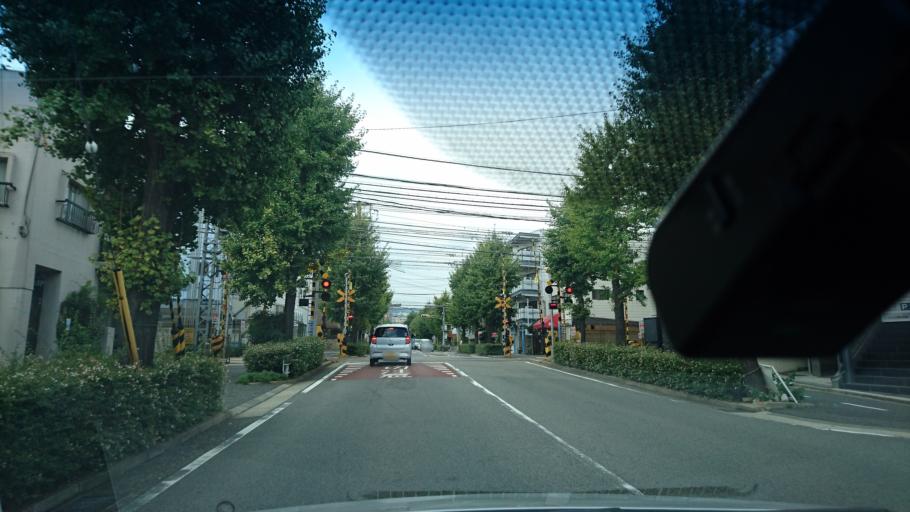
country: JP
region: Hyogo
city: Ashiya
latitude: 34.7318
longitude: 135.3169
